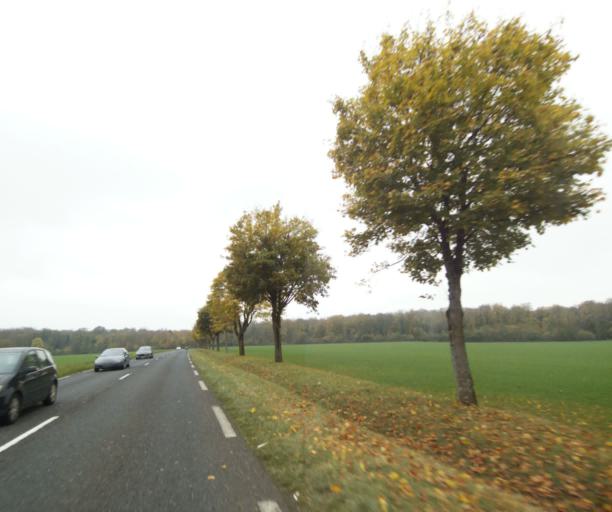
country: FR
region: Lorraine
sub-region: Departement de Meurthe-et-Moselle
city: Briey
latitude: 49.2775
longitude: 5.9593
